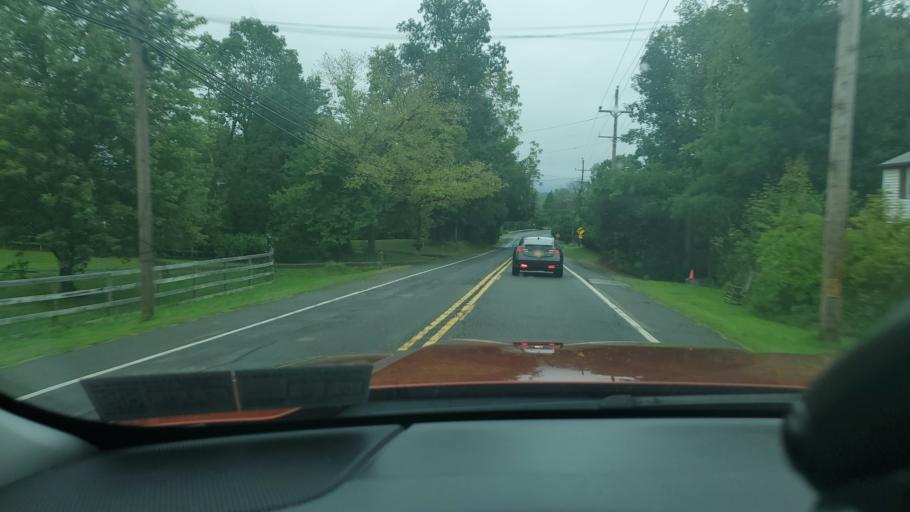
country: US
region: Pennsylvania
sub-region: Montgomery County
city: Woxall
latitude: 40.3179
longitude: -75.4818
